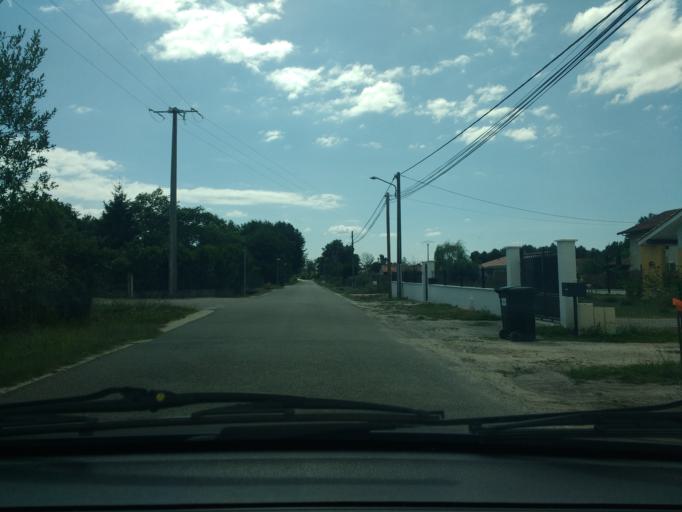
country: FR
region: Aquitaine
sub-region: Departement de la Gironde
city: Salles
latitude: 44.5631
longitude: -0.8460
